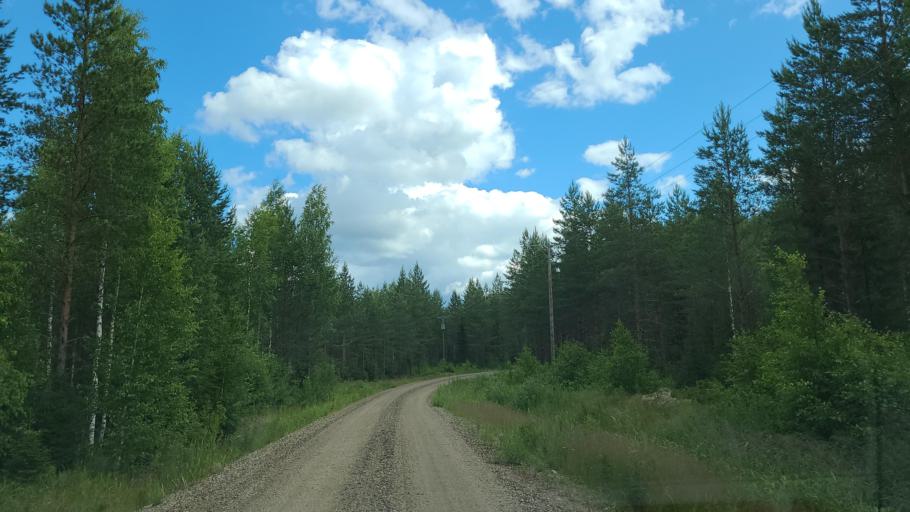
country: FI
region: Northern Savo
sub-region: Koillis-Savo
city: Kaavi
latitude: 63.0414
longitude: 28.8097
